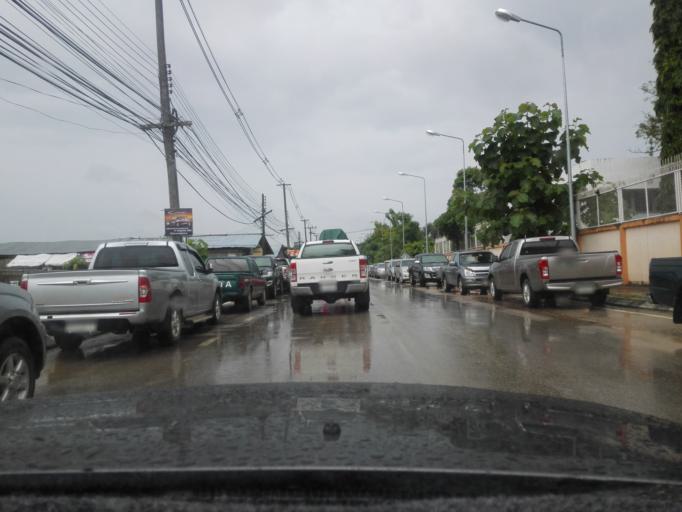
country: TH
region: Tak
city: Mae Sot
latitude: 16.7112
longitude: 98.5744
